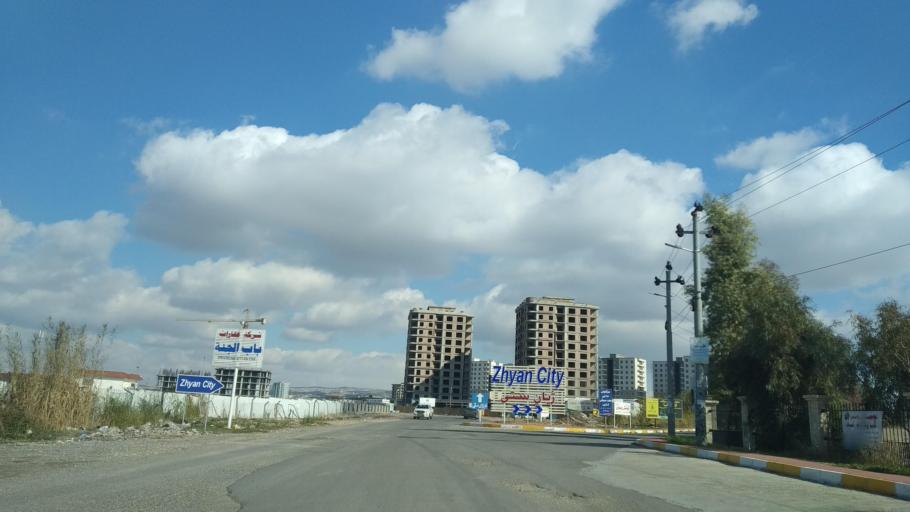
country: IQ
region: Arbil
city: Erbil
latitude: 36.2124
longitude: 44.1359
